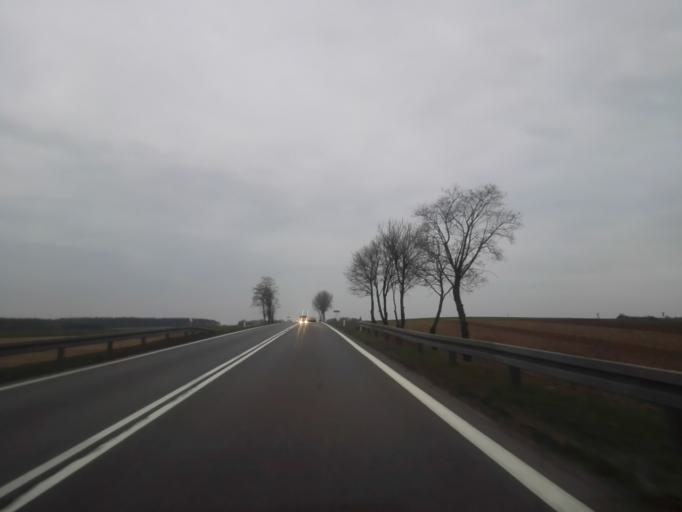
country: PL
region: Podlasie
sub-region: Powiat kolnenski
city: Stawiski
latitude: 53.4254
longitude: 22.1686
